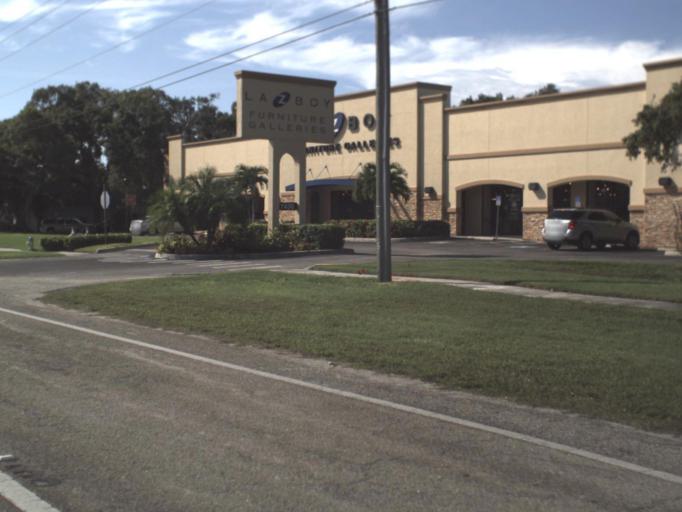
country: US
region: Florida
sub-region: Sarasota County
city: Gulf Gate Estates
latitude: 27.2469
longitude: -82.5119
